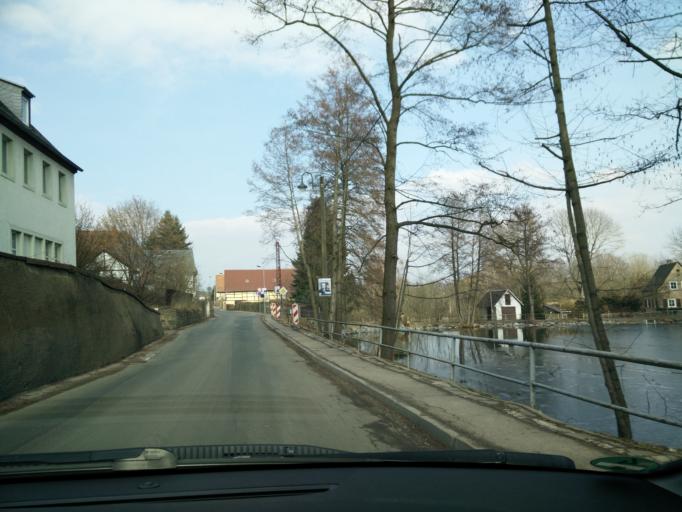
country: DE
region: Saxony
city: Colditz
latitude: 51.1188
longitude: 12.7876
